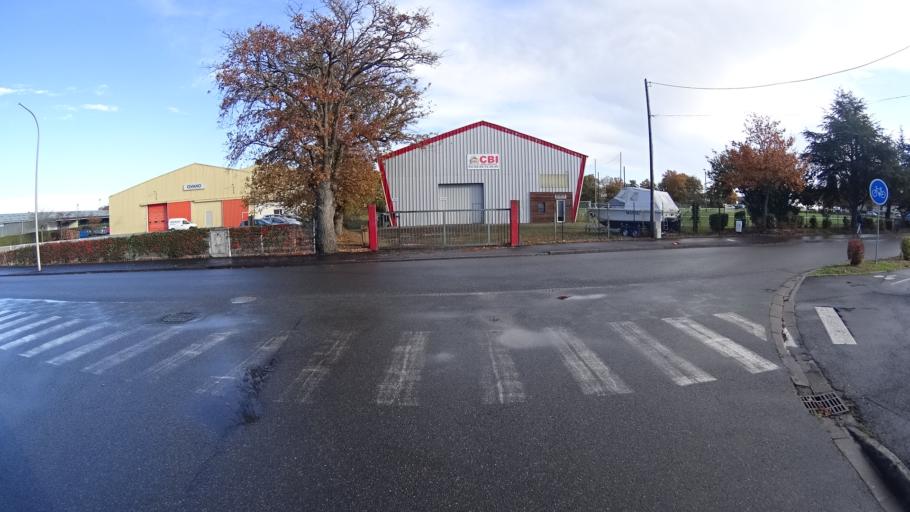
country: FR
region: Brittany
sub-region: Departement d'Ille-et-Vilaine
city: Redon
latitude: 47.6641
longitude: -2.0749
